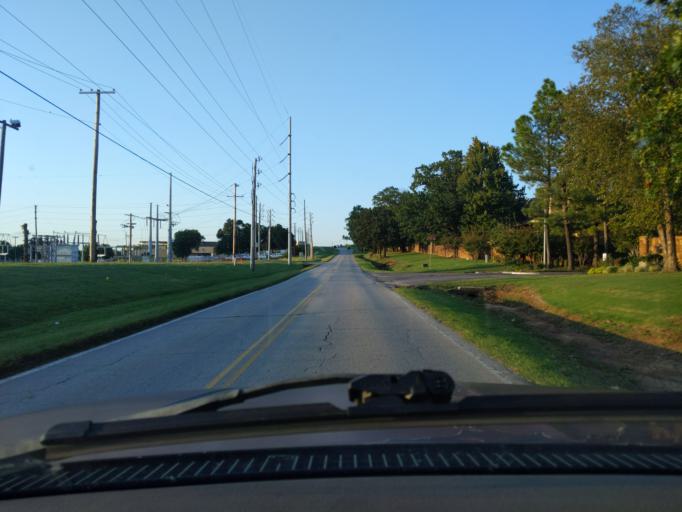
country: US
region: Oklahoma
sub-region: Tulsa County
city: Jenks
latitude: 36.0409
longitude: -95.9489
